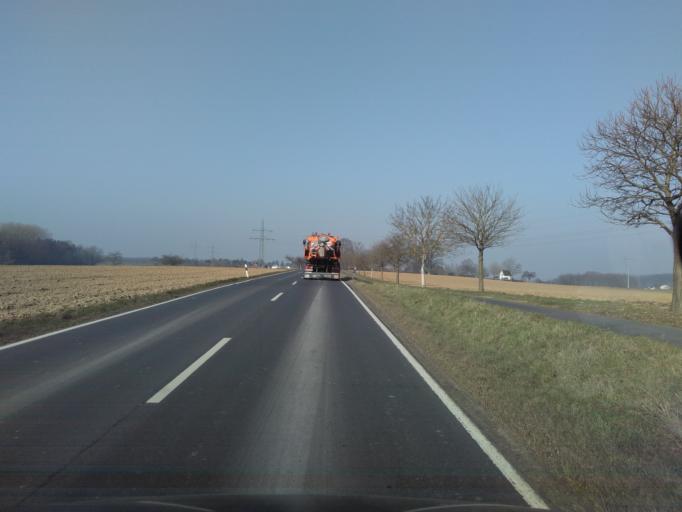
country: DE
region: Rheinland-Pfalz
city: Bannberscheid
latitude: 50.4610
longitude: 7.8407
